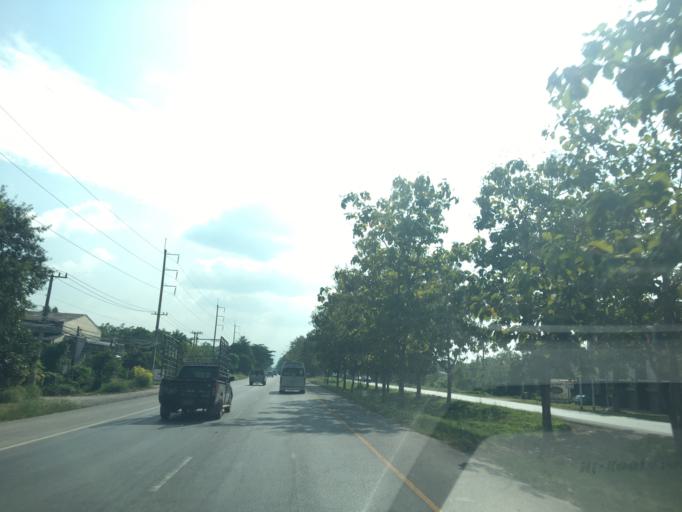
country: TH
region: Chiang Rai
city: Mae Lao
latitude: 19.7414
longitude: 99.7240
